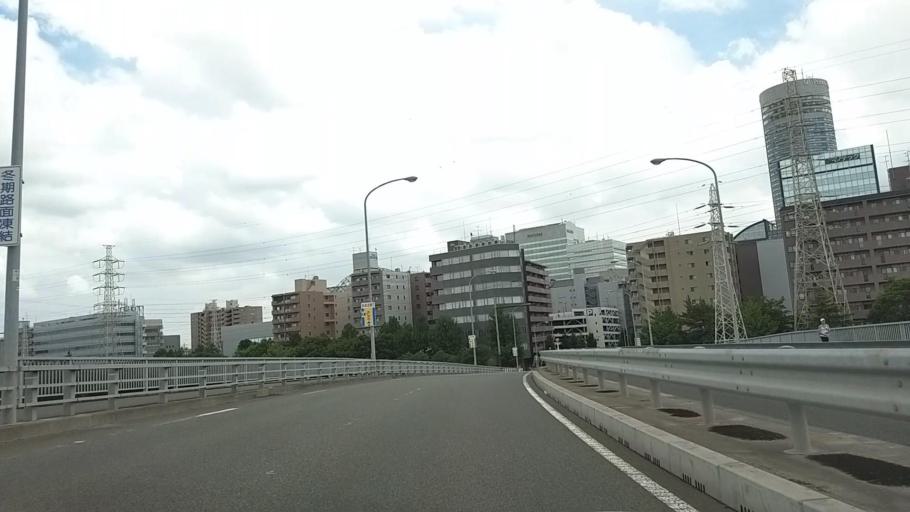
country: JP
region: Kanagawa
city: Yokohama
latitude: 35.5129
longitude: 139.6157
